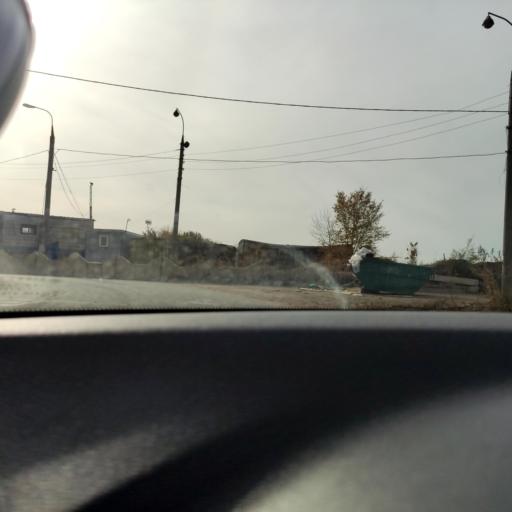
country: RU
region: Samara
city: Samara
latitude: 53.1851
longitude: 50.2299
